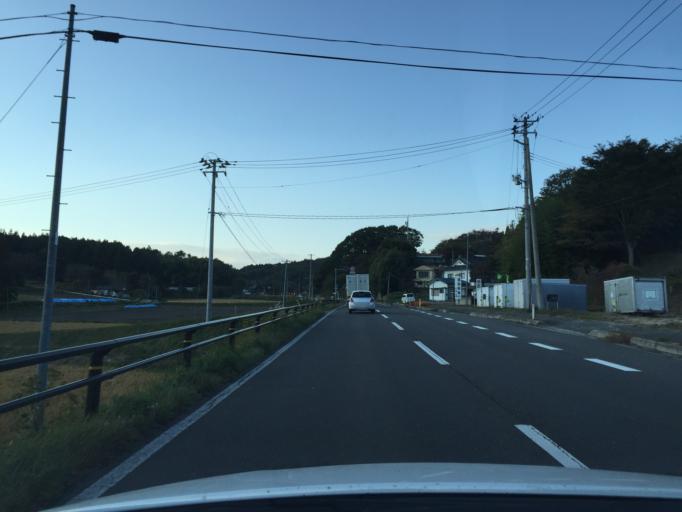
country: JP
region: Fukushima
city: Ishikawa
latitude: 37.2651
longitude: 140.5551
